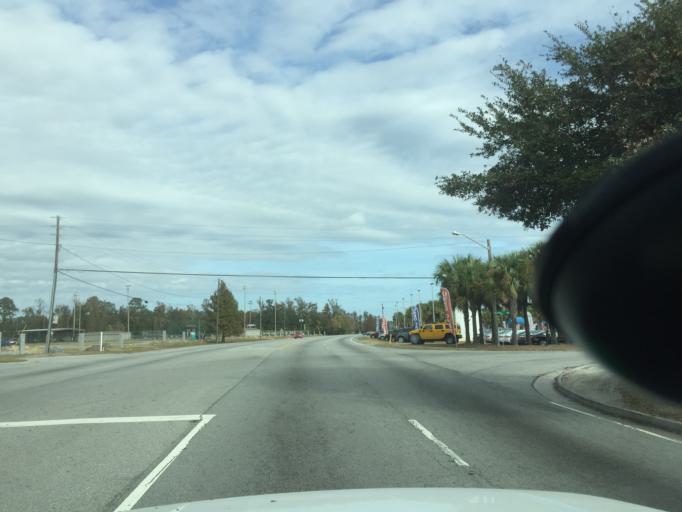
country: US
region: Georgia
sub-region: Chatham County
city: Garden City
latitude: 32.0732
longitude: -81.1606
